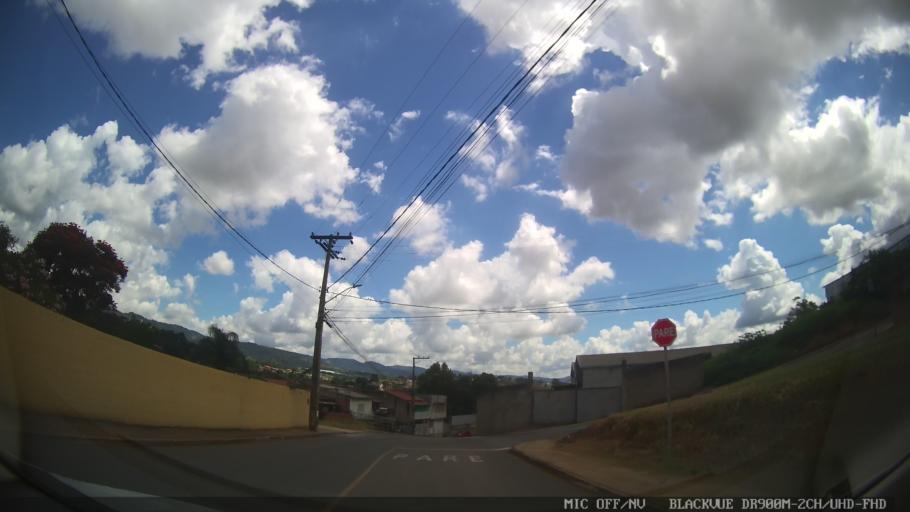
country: BR
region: Minas Gerais
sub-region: Extrema
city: Extrema
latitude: -22.8642
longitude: -46.3330
